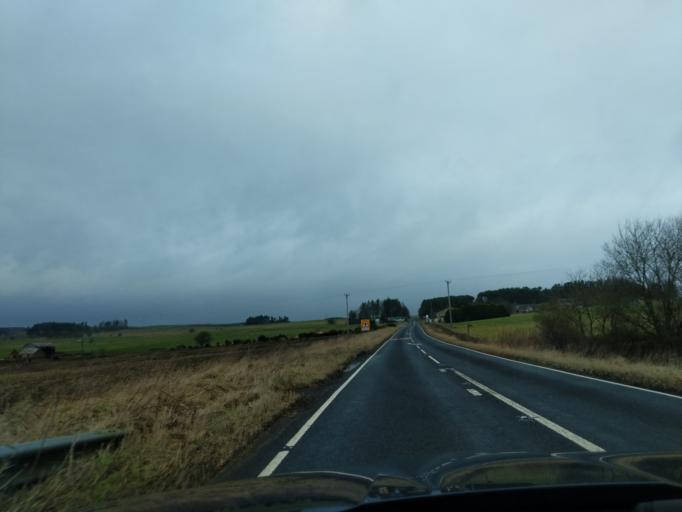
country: GB
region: England
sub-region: Northumberland
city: Rothley
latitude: 55.1623
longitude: -2.0169
